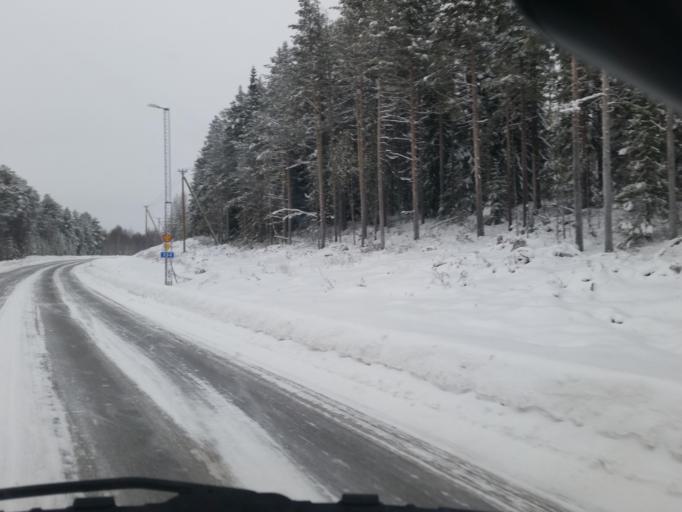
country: SE
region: Norrbotten
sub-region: Pitea Kommun
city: Bergsviken
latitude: 65.3857
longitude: 21.3276
